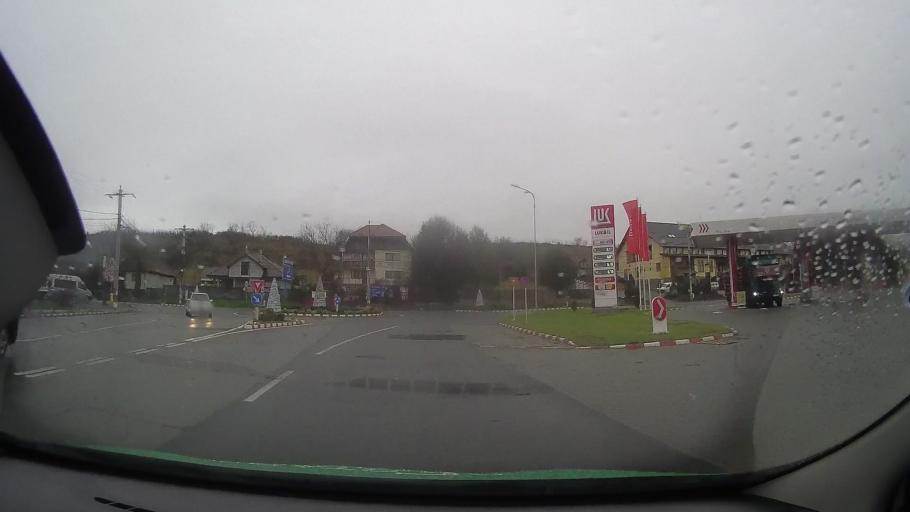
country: RO
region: Mures
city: Reghin-Sat
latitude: 46.7910
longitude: 24.7141
